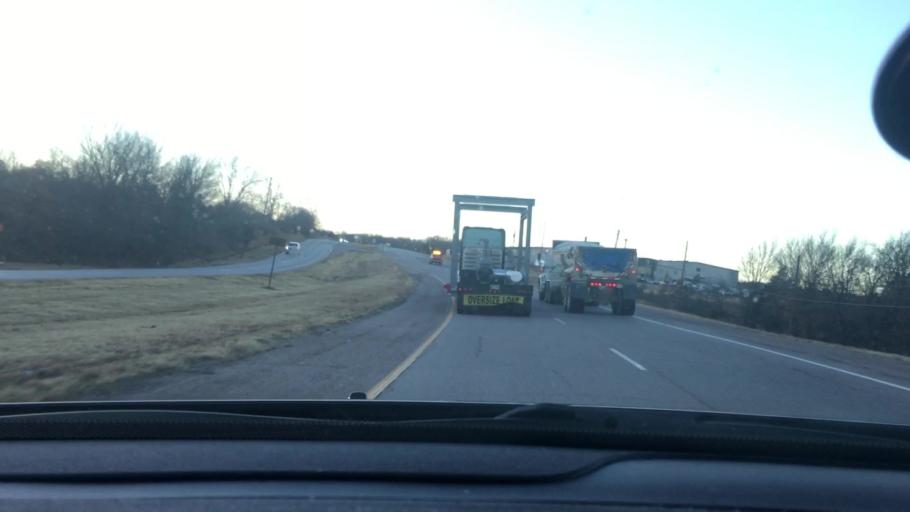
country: US
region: Oklahoma
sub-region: Pontotoc County
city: Ada
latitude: 34.7403
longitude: -96.7092
